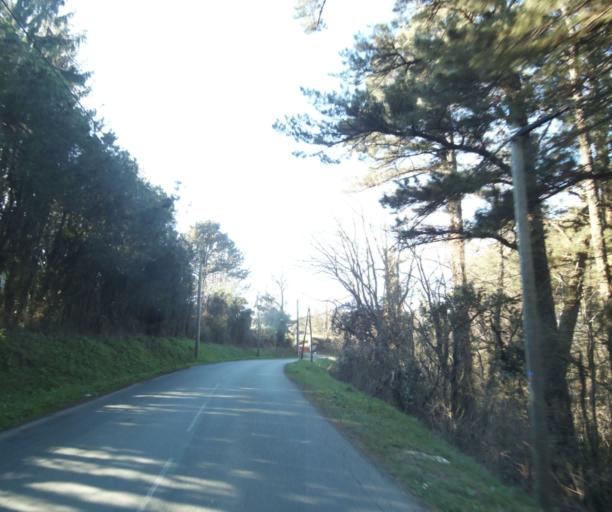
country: FR
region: Aquitaine
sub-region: Departement des Pyrenees-Atlantiques
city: Hendaye
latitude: 43.3536
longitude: -1.7409
